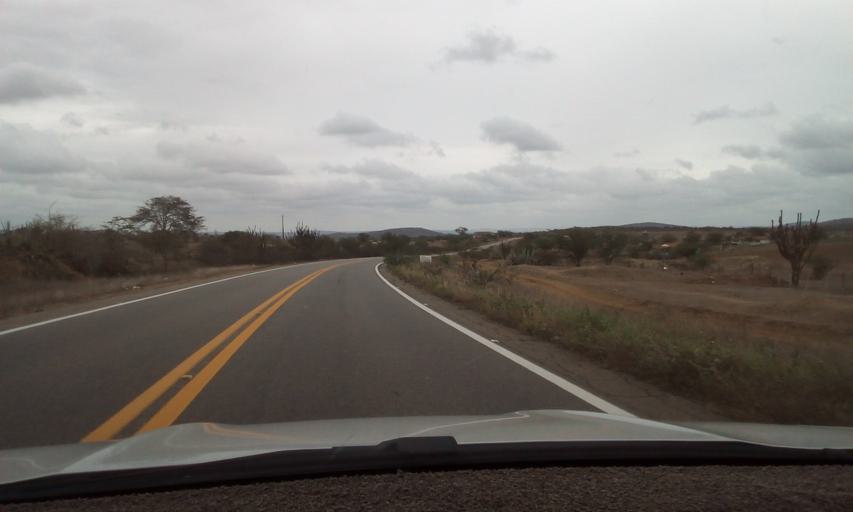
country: BR
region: Paraiba
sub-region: Areia
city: Remigio
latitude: -6.9067
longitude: -35.8760
